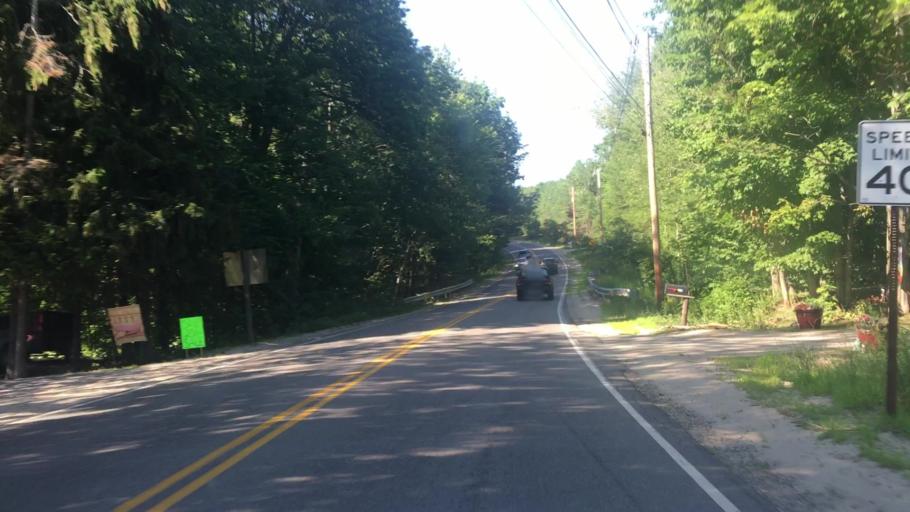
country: US
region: Maine
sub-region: York County
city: Hollis Center
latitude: 43.6798
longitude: -70.5878
